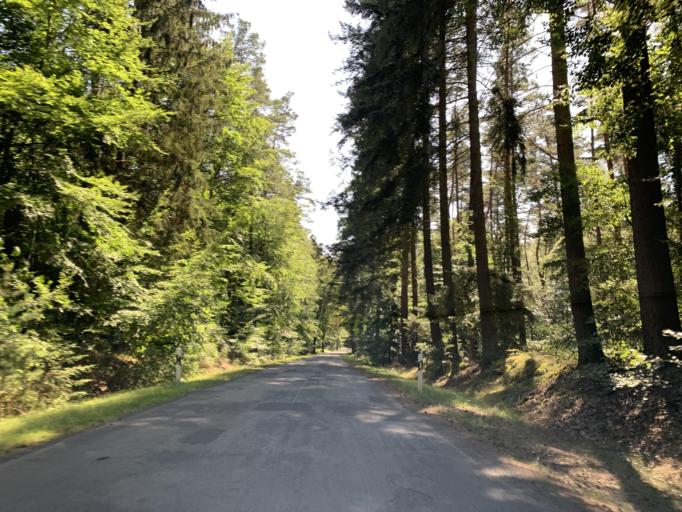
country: DE
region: Mecklenburg-Vorpommern
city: Carpin
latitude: 53.3383
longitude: 13.2427
